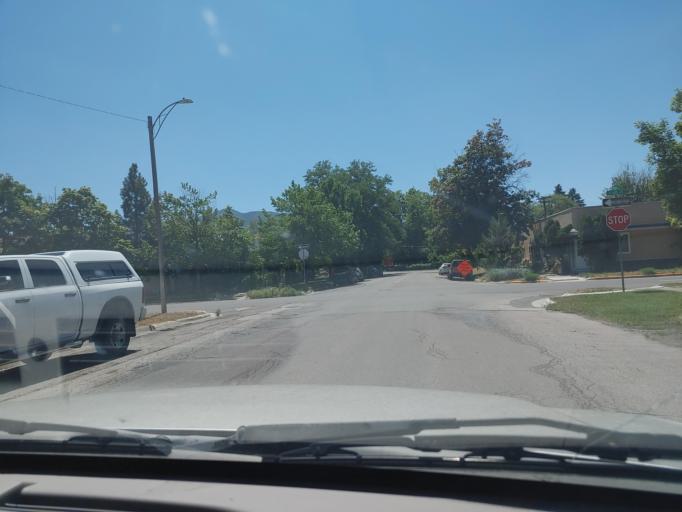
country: US
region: Montana
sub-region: Missoula County
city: Missoula
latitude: 46.8643
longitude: -114.0081
